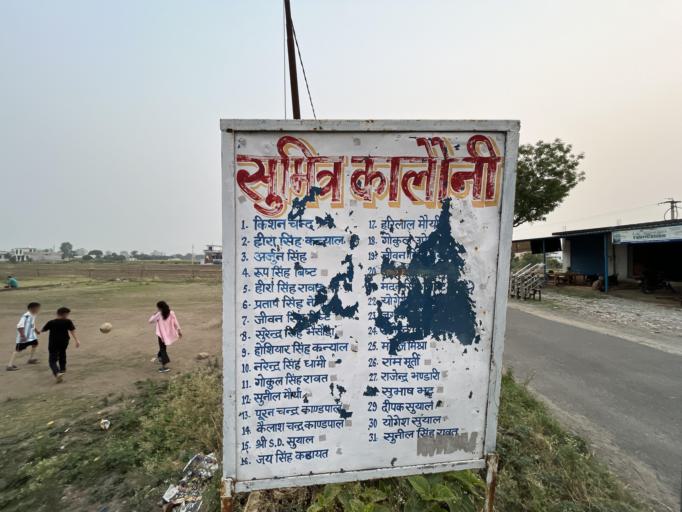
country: IN
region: Uttarakhand
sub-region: Naini Tal
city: Haldwani
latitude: 29.1649
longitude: 79.4786
